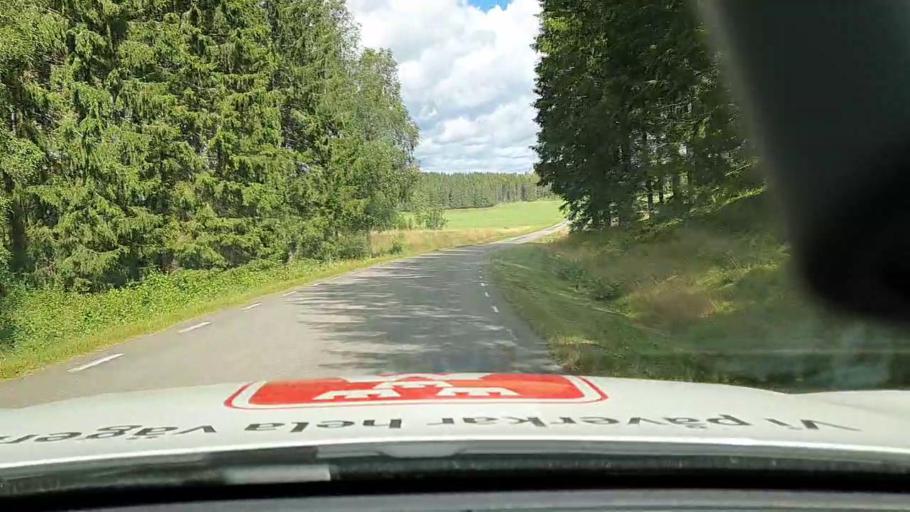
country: SE
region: Vaestra Goetaland
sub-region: Karlsborgs Kommun
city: Molltorp
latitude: 58.6088
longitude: 14.3201
